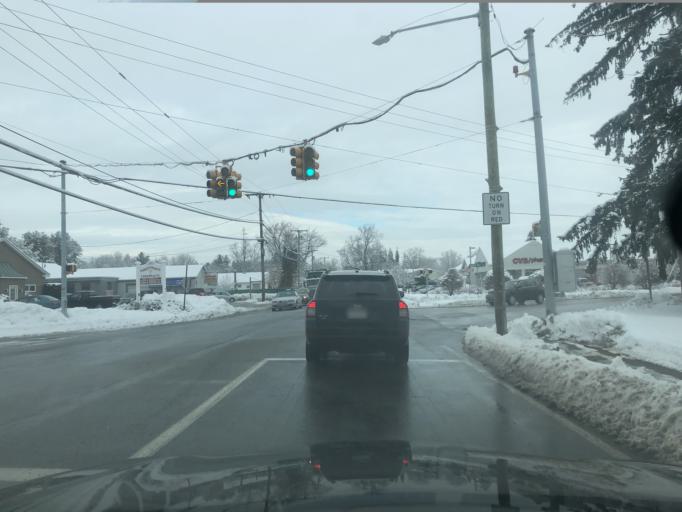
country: US
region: New Hampshire
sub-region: Strafford County
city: Somersworth
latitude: 43.2472
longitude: -70.8743
